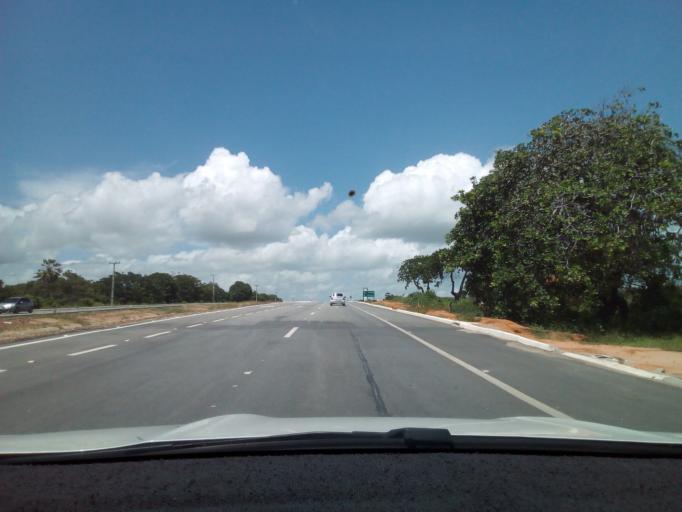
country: BR
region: Ceara
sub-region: Aracati
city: Aracati
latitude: -4.5110
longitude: -37.8000
